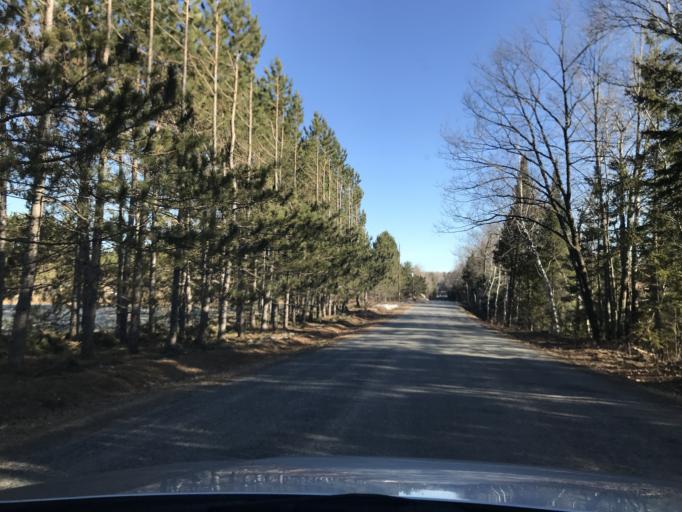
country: US
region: Wisconsin
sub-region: Marinette County
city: Niagara
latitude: 45.3604
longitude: -88.0296
